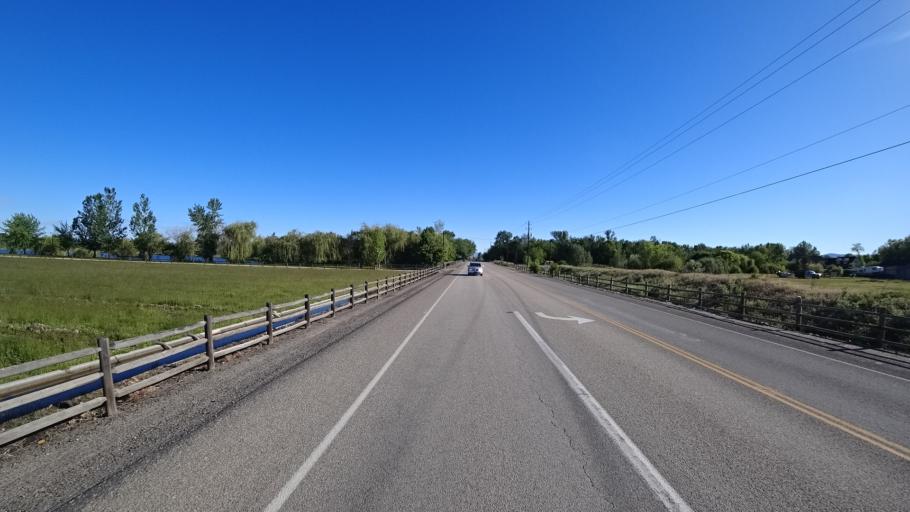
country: US
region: Idaho
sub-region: Ada County
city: Eagle
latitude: 43.6849
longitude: -116.4138
